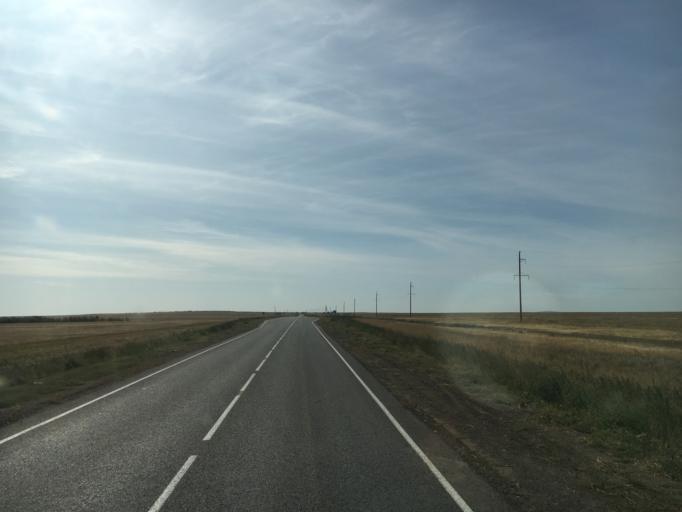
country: KZ
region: Batys Qazaqstan
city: Peremetnoe
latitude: 51.1172
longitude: 50.6291
